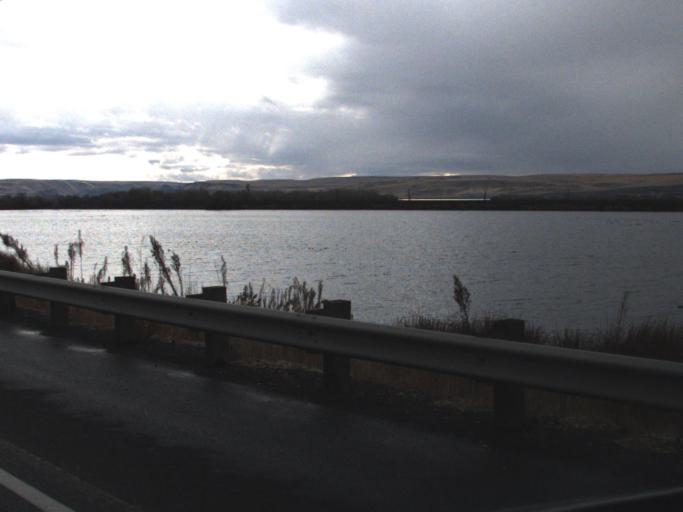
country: US
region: Washington
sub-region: Walla Walla County
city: Burbank
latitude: 46.1582
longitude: -118.9425
